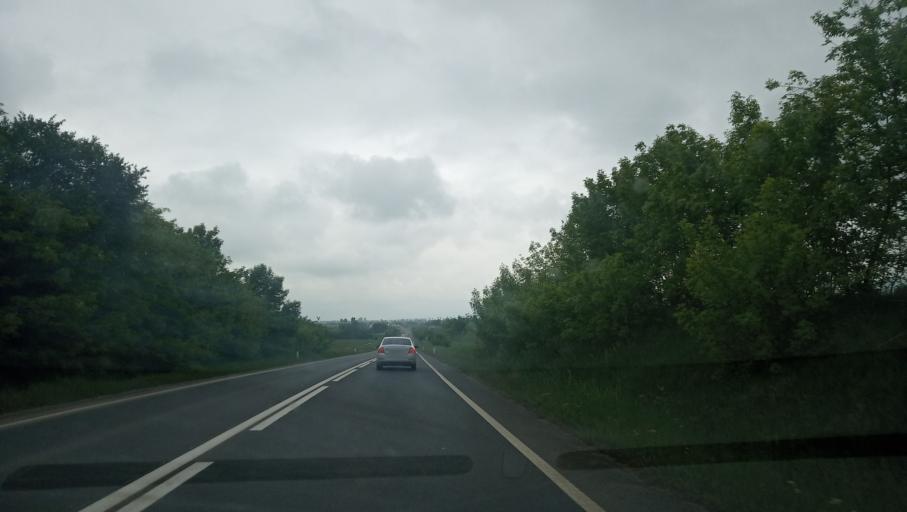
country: RO
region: Alba
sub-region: Comuna Saliste
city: Salistea
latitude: 45.9448
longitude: 23.4013
